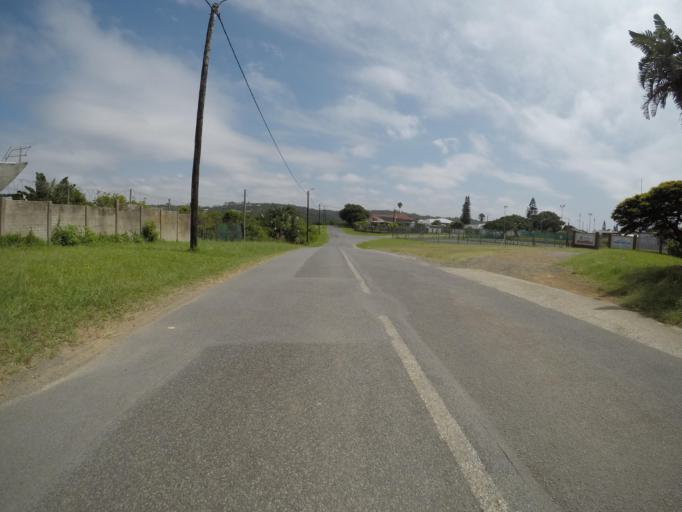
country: ZA
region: Eastern Cape
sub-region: Buffalo City Metropolitan Municipality
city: East London
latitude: -32.9382
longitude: 28.0237
